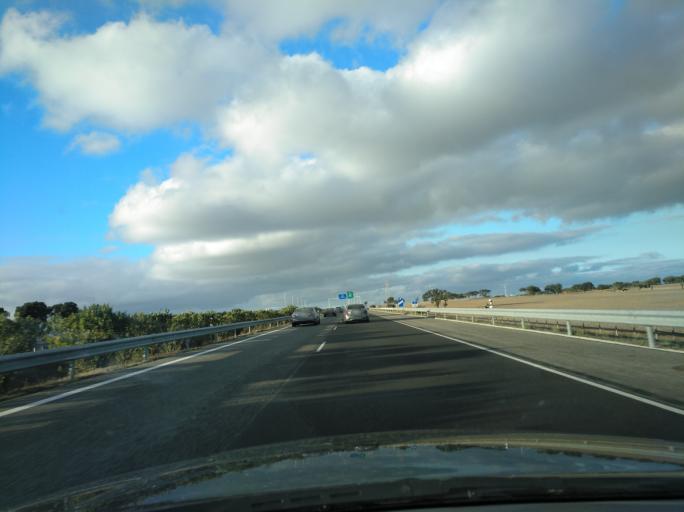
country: PT
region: Beja
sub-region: Ourique
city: Ourique
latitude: 37.6579
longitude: -8.1563
